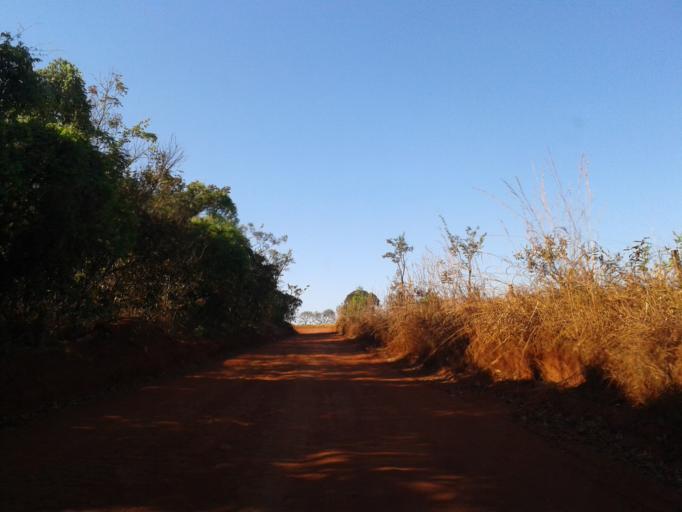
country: BR
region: Minas Gerais
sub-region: Ituiutaba
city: Ituiutaba
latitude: -19.0009
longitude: -49.3697
